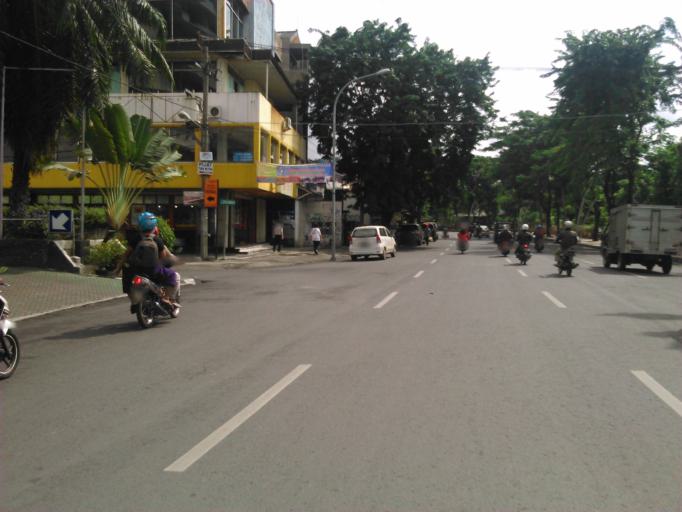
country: ID
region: East Java
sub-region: Kota Surabaya
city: Surabaya
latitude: -7.2589
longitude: 112.7430
